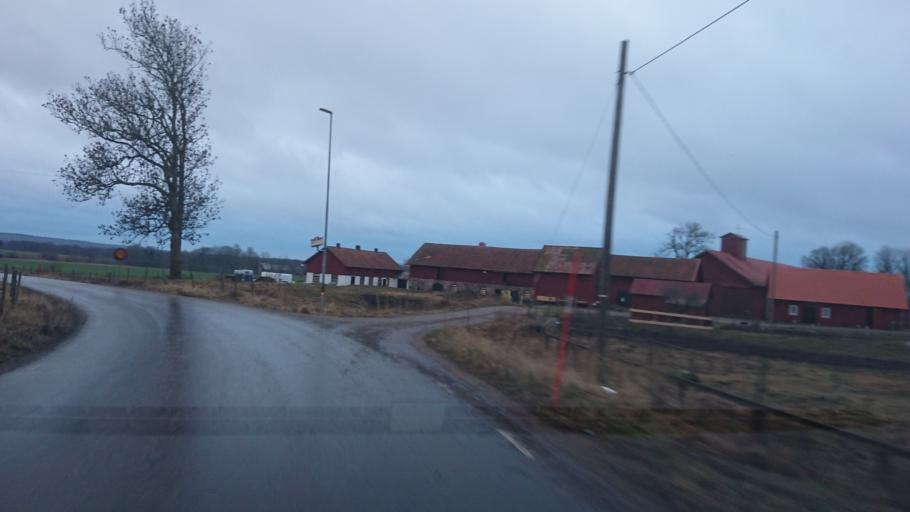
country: SE
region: Uppsala
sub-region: Uppsala Kommun
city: Gamla Uppsala
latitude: 59.9548
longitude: 17.6054
